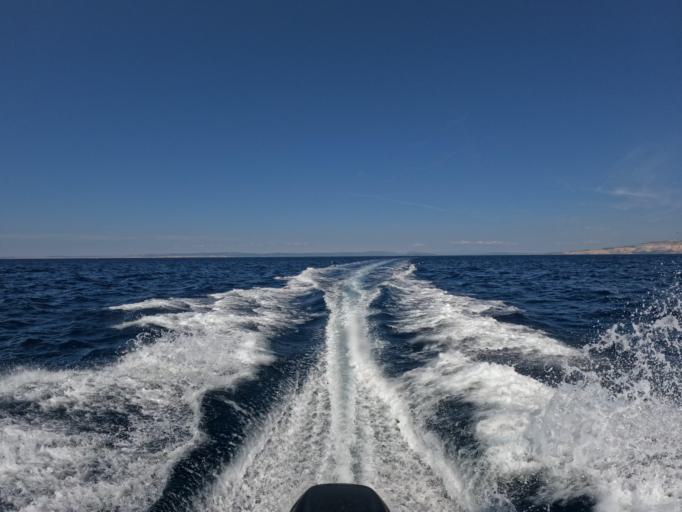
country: HR
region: Primorsko-Goranska
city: Lopar
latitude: 44.8575
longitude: 14.6965
